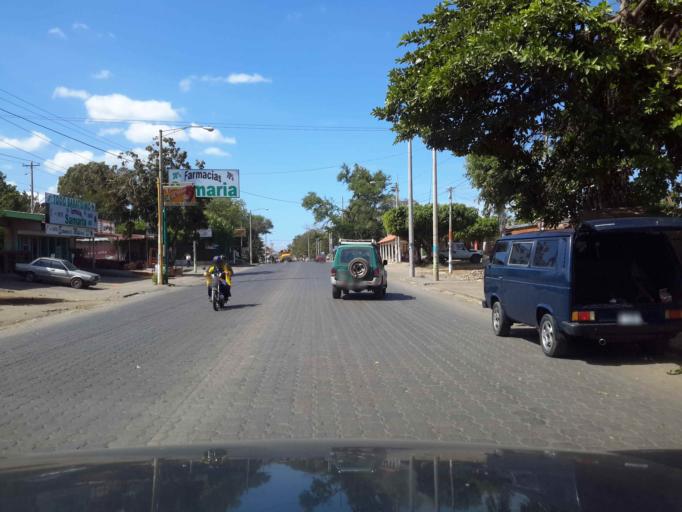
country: NI
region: Managua
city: Managua
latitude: 12.1277
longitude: -86.2111
